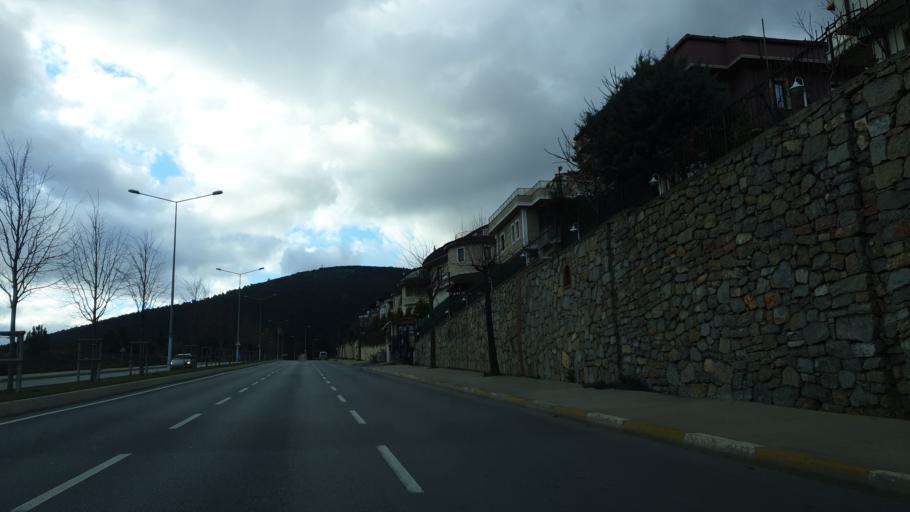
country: TR
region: Istanbul
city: Sultanbeyli
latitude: 40.9221
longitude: 29.2683
